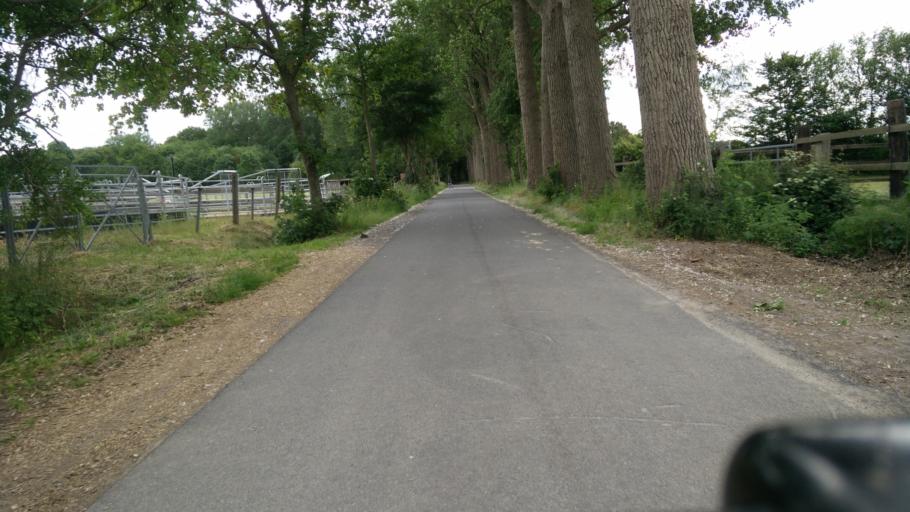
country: DE
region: Lower Saxony
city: Hagenburg
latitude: 52.4465
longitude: 9.3714
